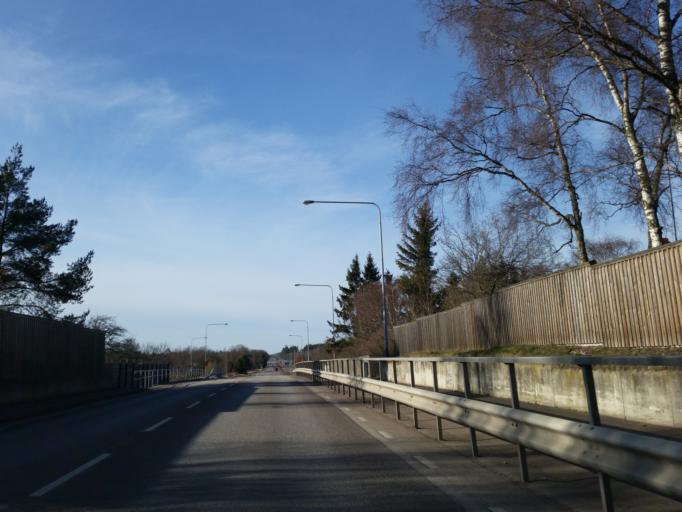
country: SE
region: Kalmar
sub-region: Kalmar Kommun
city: Lindsdal
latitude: 56.7020
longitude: 16.3252
